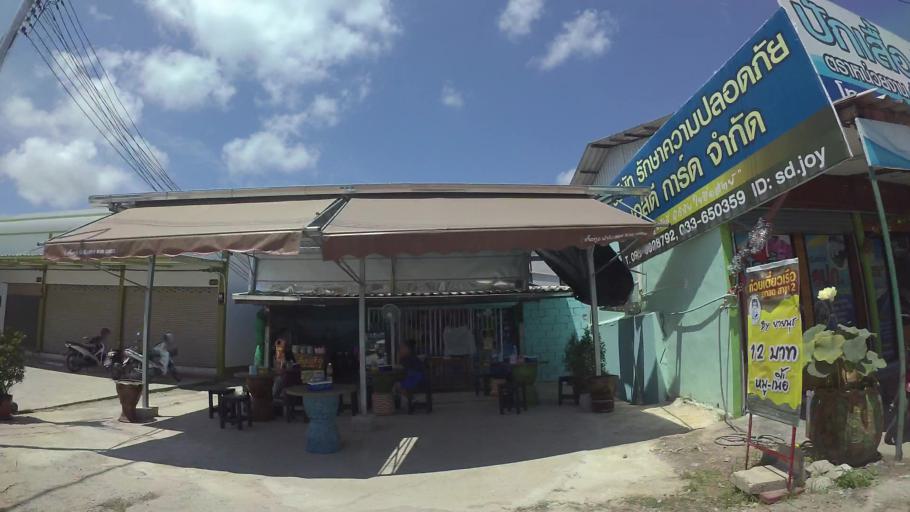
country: TH
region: Rayong
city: Rayong
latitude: 12.6910
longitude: 101.2691
